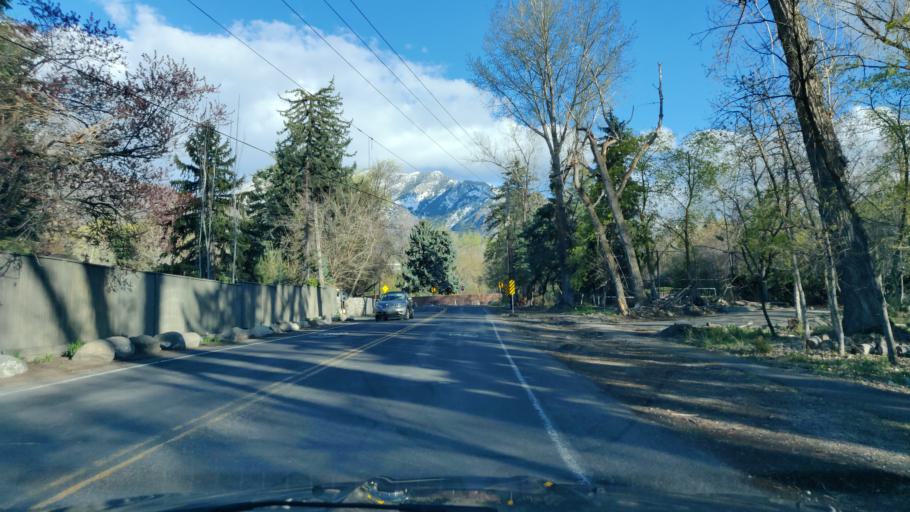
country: US
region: Utah
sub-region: Salt Lake County
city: Cottonwood Heights
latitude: 40.6383
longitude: -111.8143
